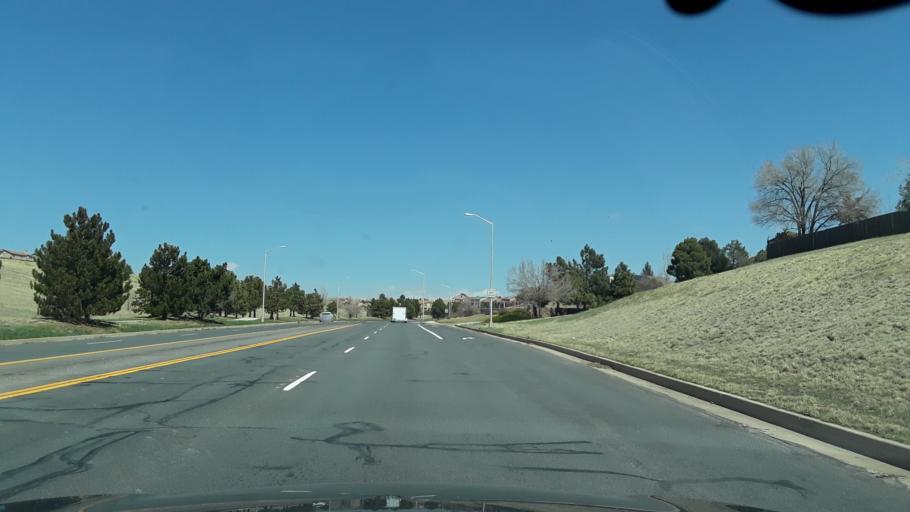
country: US
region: Colorado
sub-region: El Paso County
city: Black Forest
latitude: 38.9482
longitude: -104.7424
